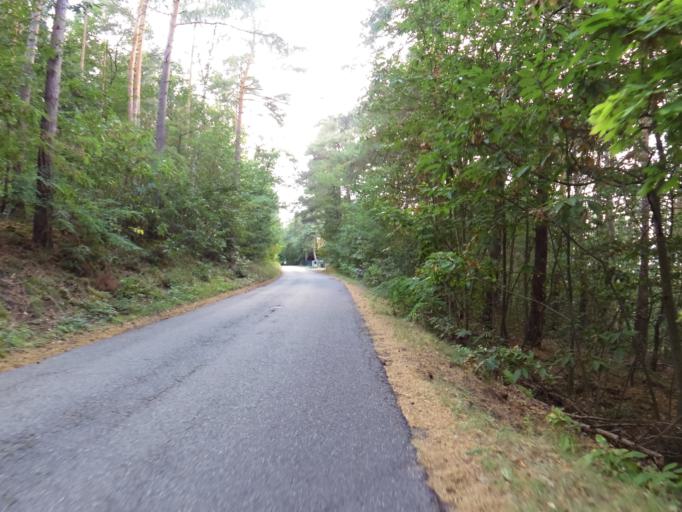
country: DE
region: Rheinland-Pfalz
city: Bad Duerkheim
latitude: 49.4516
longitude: 8.1424
